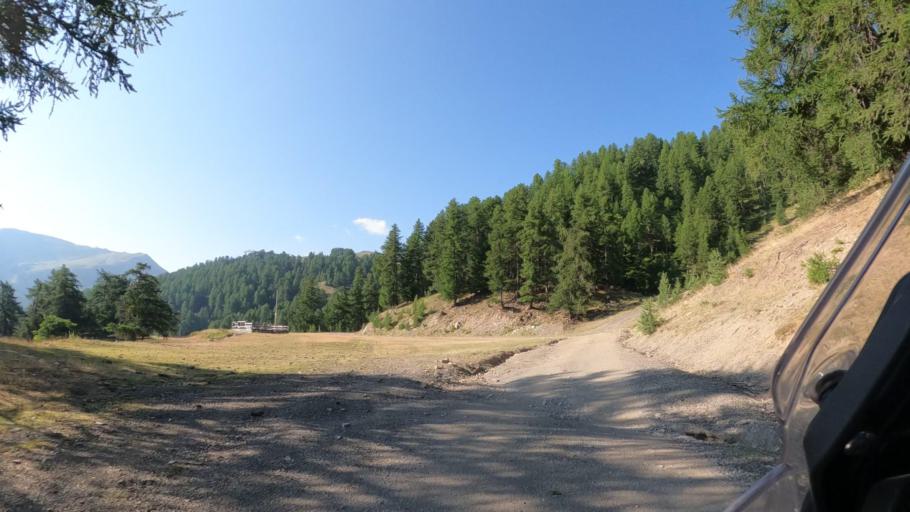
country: FR
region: Provence-Alpes-Cote d'Azur
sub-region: Departement des Hautes-Alpes
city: Guillestre
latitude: 44.6130
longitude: 6.6243
